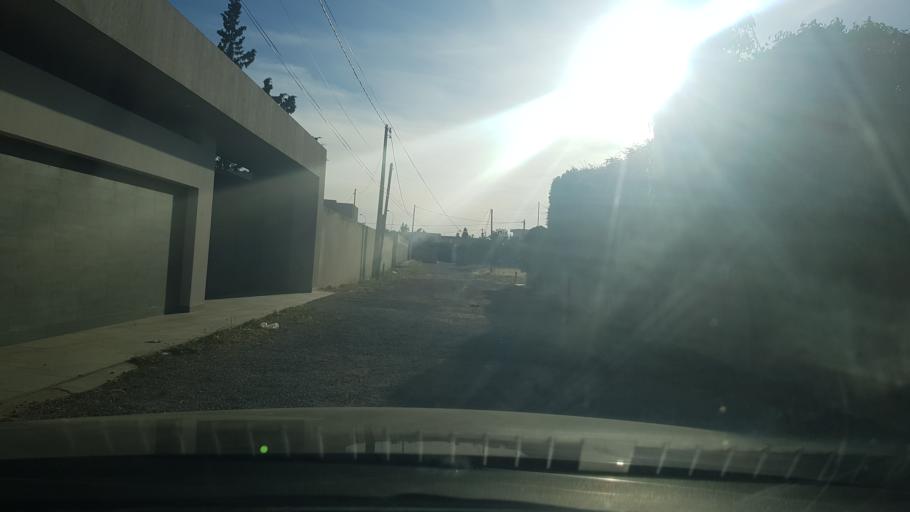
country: TN
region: Safaqis
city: Al Qarmadah
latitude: 34.8295
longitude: 10.7630
